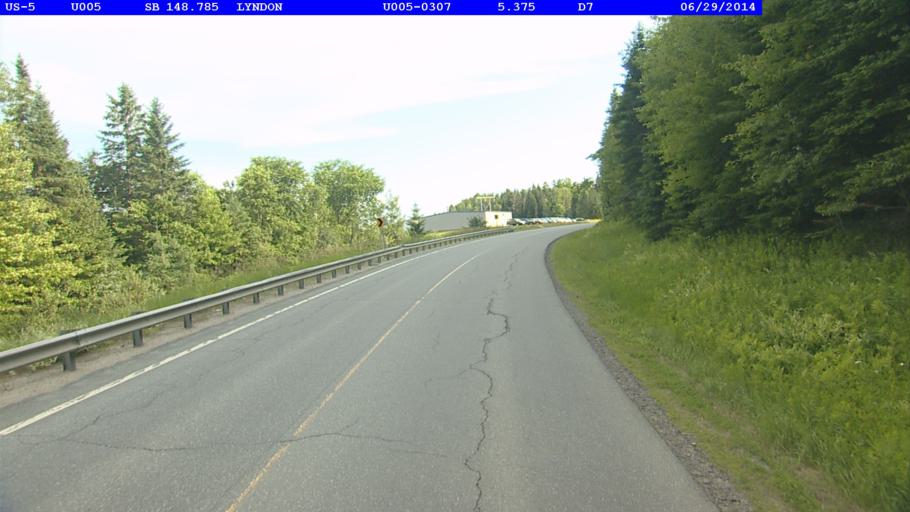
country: US
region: Vermont
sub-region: Caledonia County
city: Lyndonville
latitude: 44.5650
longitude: -71.9893
